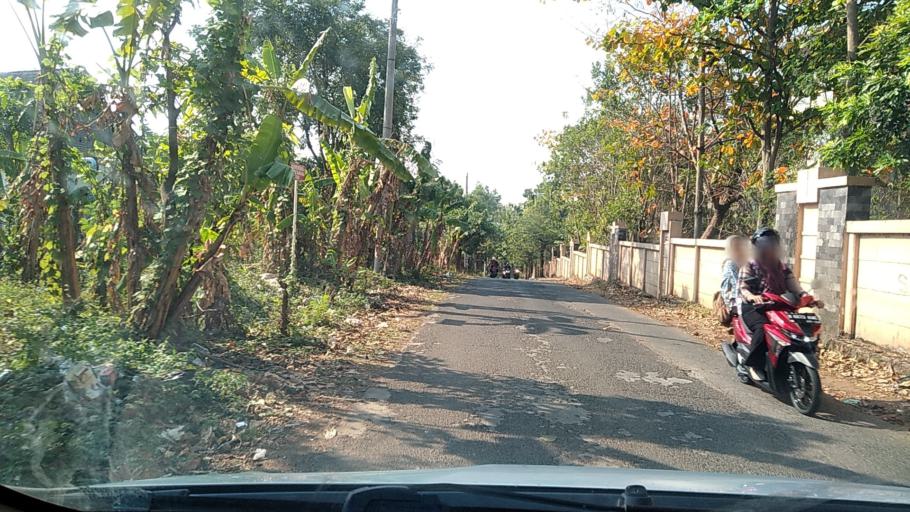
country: ID
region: Central Java
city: Semarang
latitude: -7.0559
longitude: 110.4435
